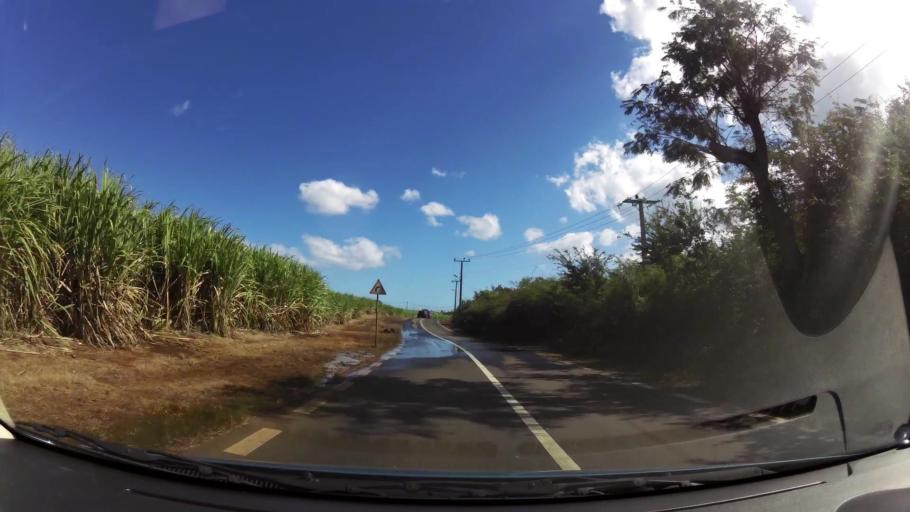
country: MU
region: Black River
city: Gros Cailloux
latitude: -20.2218
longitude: 57.4216
